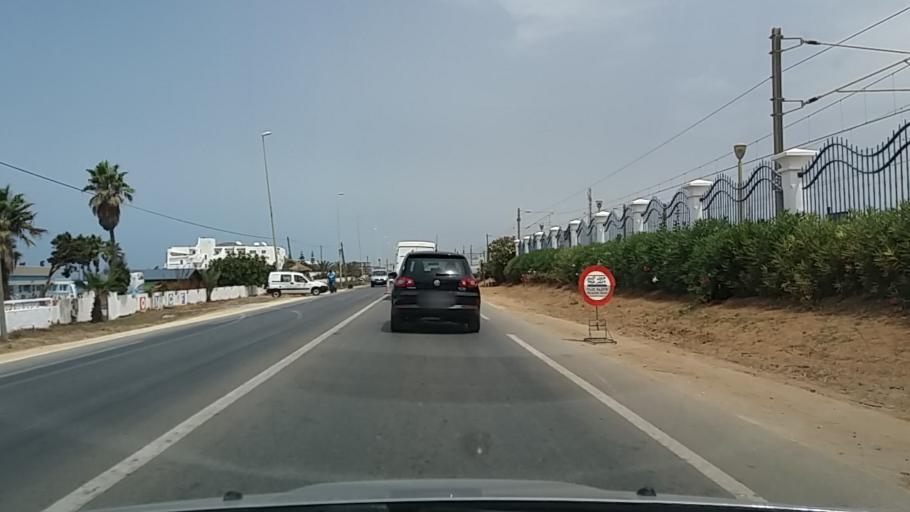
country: MA
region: Tanger-Tetouan
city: Asilah
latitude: 35.4829
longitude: -6.0238
